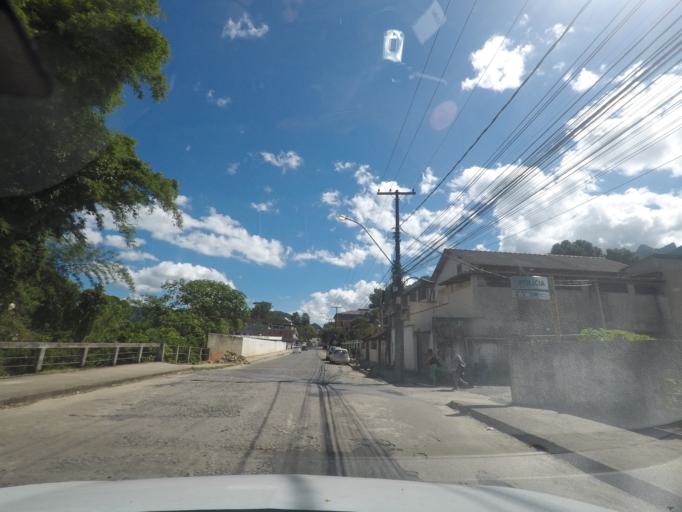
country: BR
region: Rio de Janeiro
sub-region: Teresopolis
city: Teresopolis
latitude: -22.4392
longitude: -42.9774
